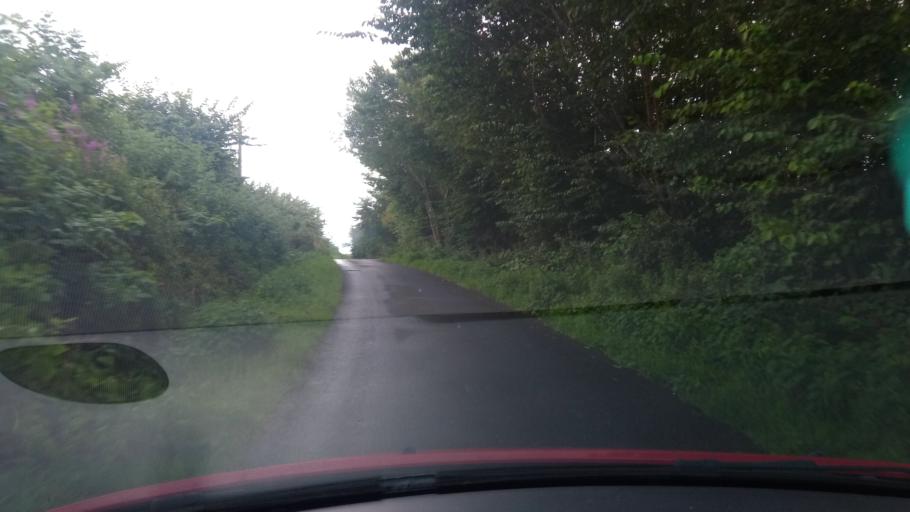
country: GB
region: Scotland
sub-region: The Scottish Borders
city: Hawick
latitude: 55.4191
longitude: -2.7806
